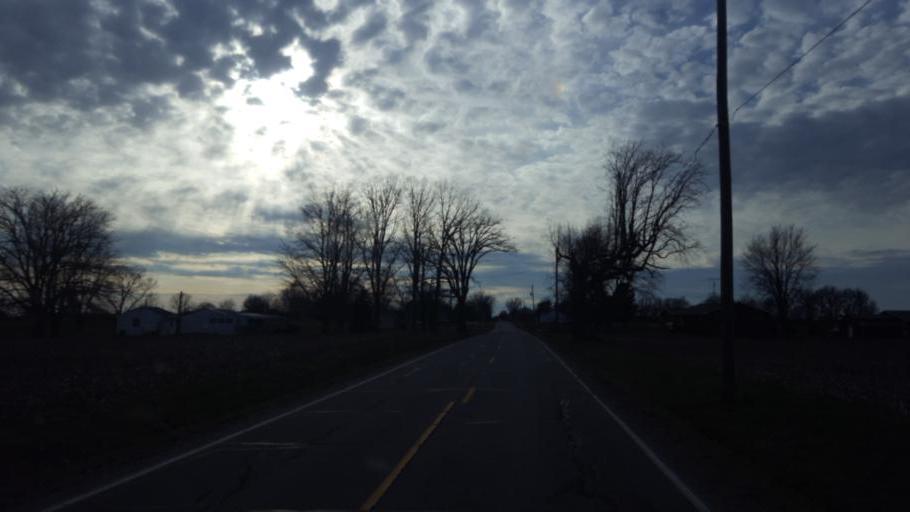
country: US
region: Ohio
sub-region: Crawford County
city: Bucyrus
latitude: 40.7888
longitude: -82.9391
